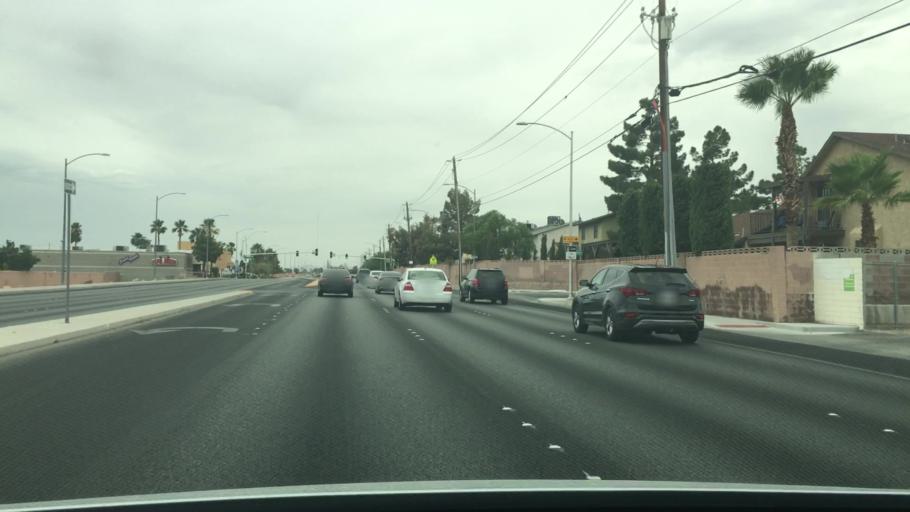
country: US
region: Nevada
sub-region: Clark County
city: Spring Valley
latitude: 36.1685
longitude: -115.2600
